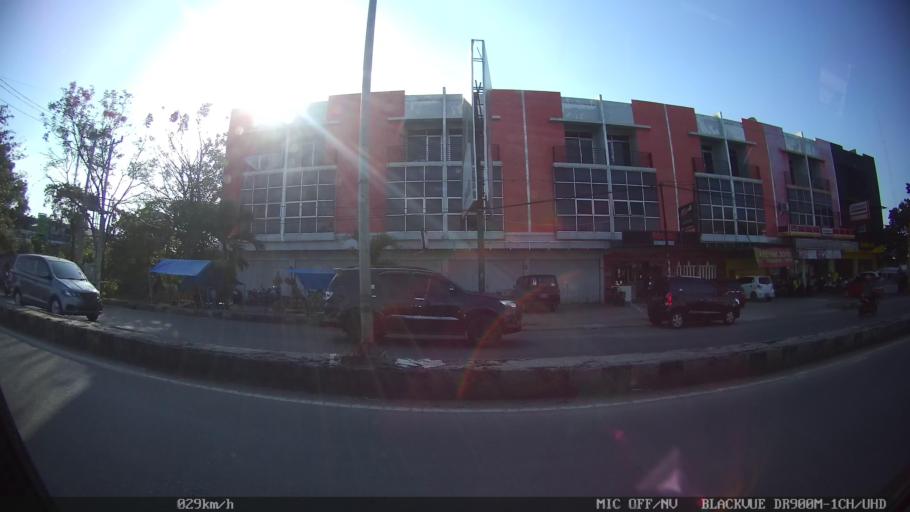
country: ID
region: Lampung
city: Kedaton
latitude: -5.3748
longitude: 105.2229
